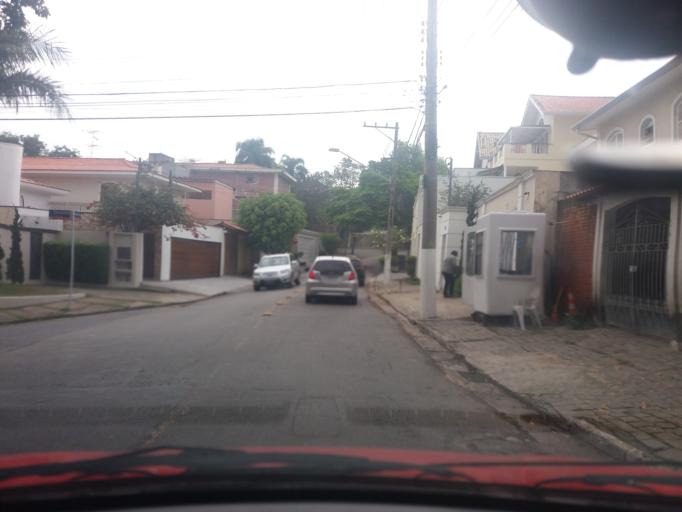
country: BR
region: Sao Paulo
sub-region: Taboao Da Serra
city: Taboao da Serra
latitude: -23.5964
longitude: -46.7245
